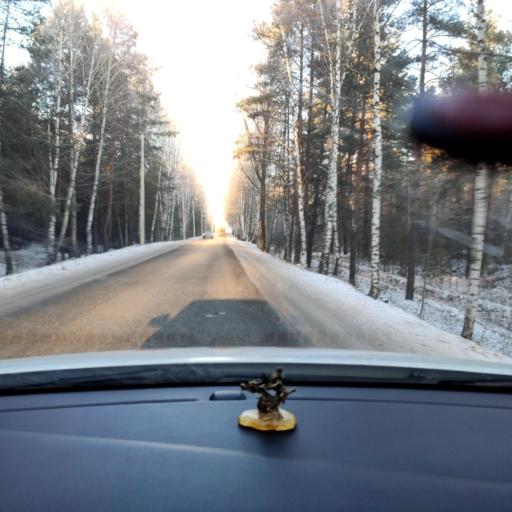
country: RU
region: Tatarstan
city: Stolbishchi
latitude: 55.6721
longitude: 49.1213
